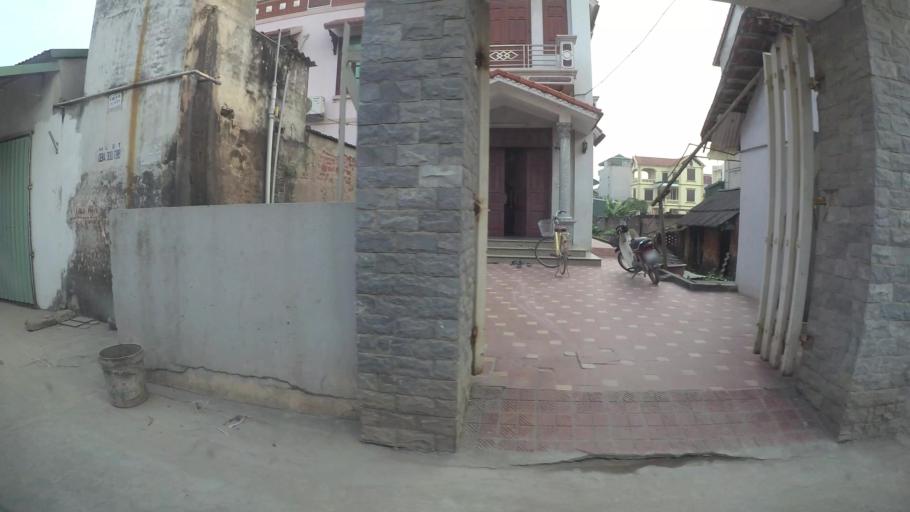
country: VN
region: Ha Noi
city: Cau Dien
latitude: 21.0061
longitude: 105.7232
